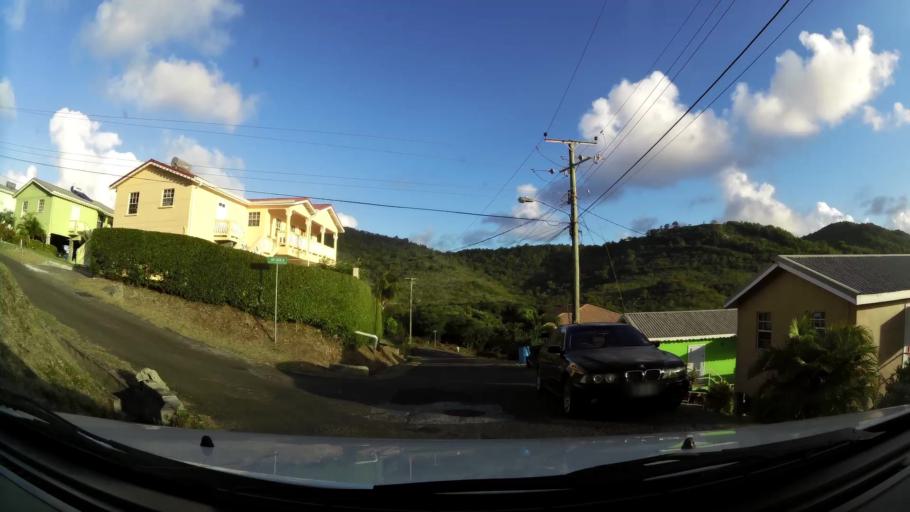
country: LC
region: Gros-Islet
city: Gros Islet
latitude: 14.0754
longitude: -60.9270
